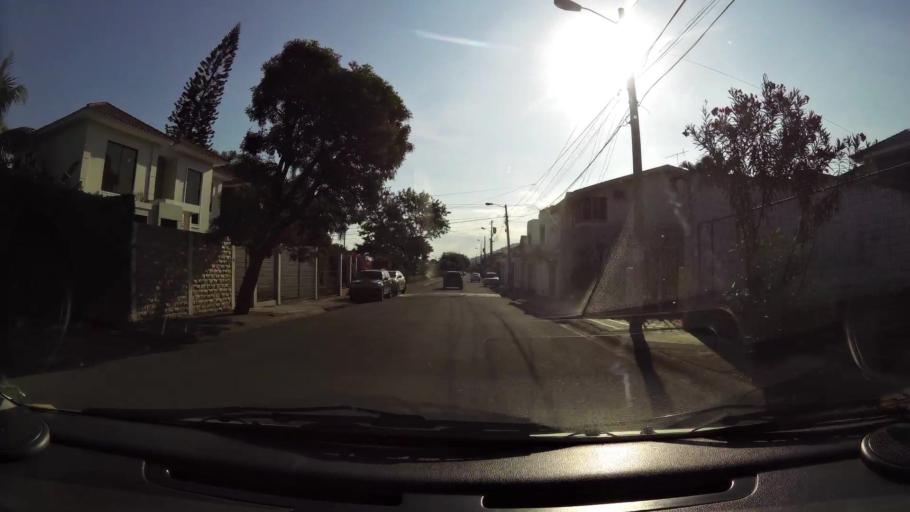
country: EC
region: Guayas
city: Santa Lucia
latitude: -2.1871
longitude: -79.9677
